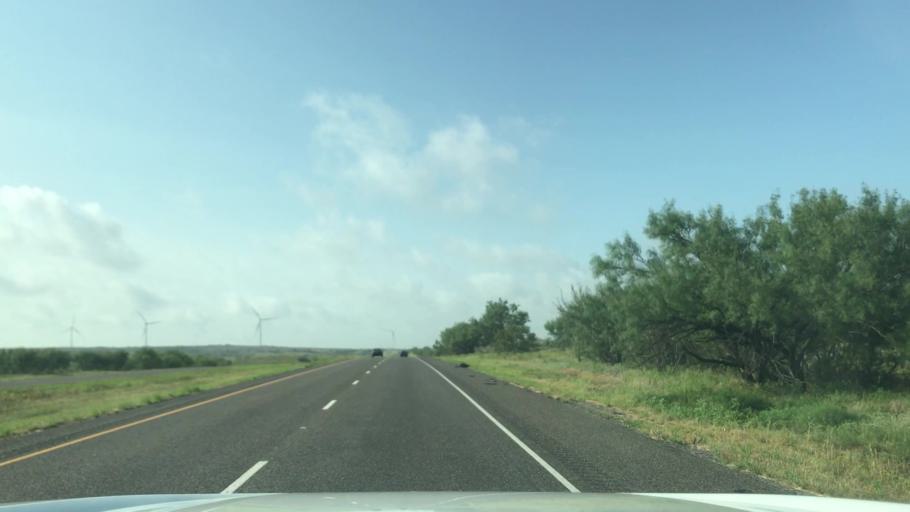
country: US
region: Texas
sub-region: Scurry County
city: Snyder
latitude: 32.9095
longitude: -101.0578
